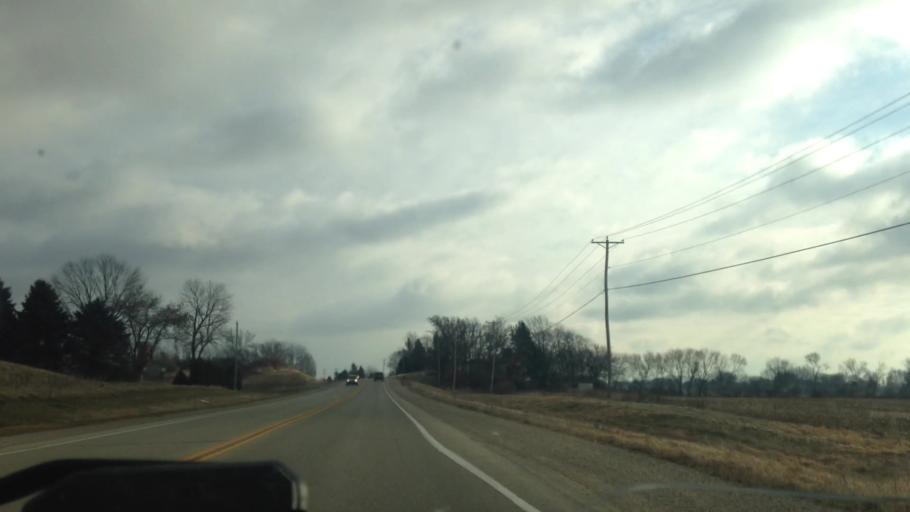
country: US
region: Wisconsin
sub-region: Dodge County
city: Beaver Dam
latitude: 43.4453
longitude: -88.7802
